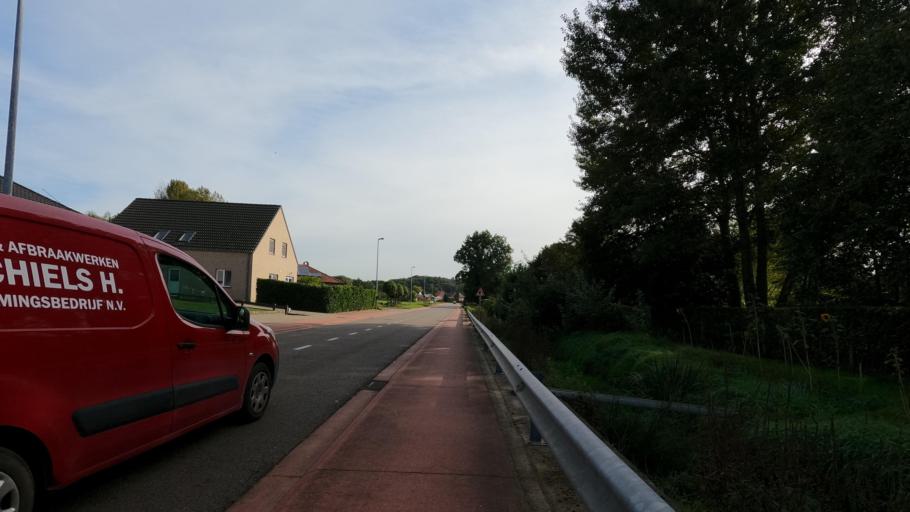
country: BE
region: Flanders
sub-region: Provincie Vlaams-Brabant
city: Scherpenheuvel-Zichem
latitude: 51.0121
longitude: 4.9421
